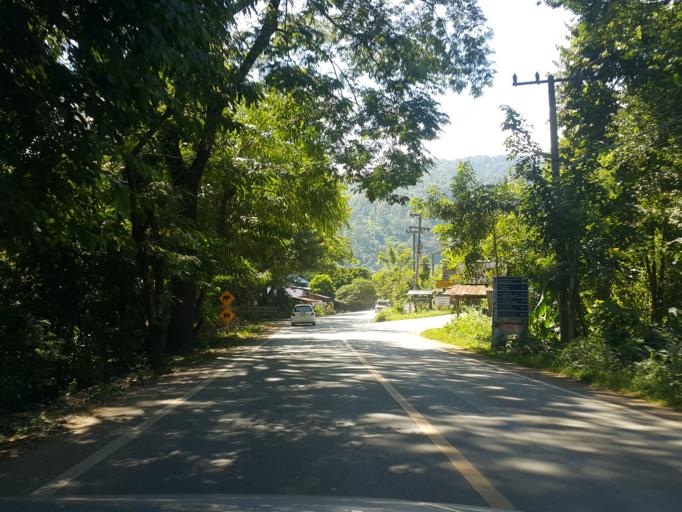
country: TH
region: Chiang Mai
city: Mae Taeng
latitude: 19.2007
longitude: 98.8902
